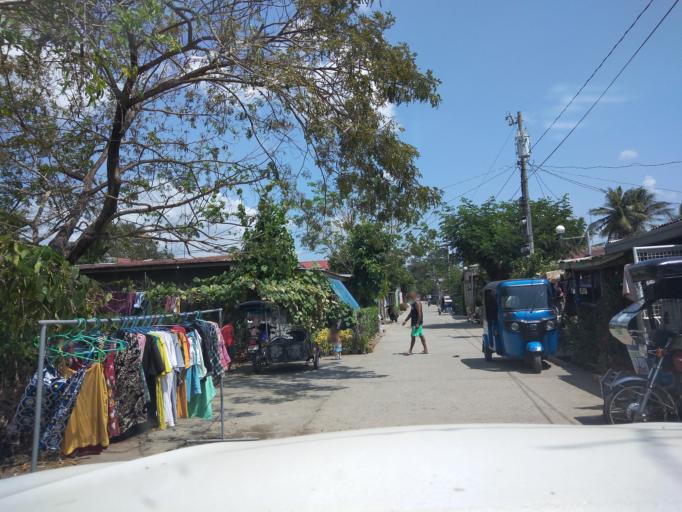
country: PH
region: Central Luzon
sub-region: Province of Pampanga
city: Bahay Pare
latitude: 15.0170
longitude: 120.8752
